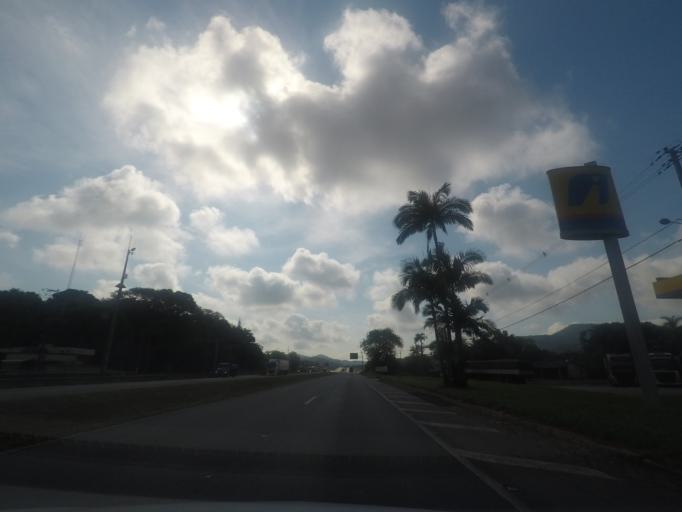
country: BR
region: Parana
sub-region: Antonina
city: Antonina
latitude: -25.5515
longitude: -48.7978
